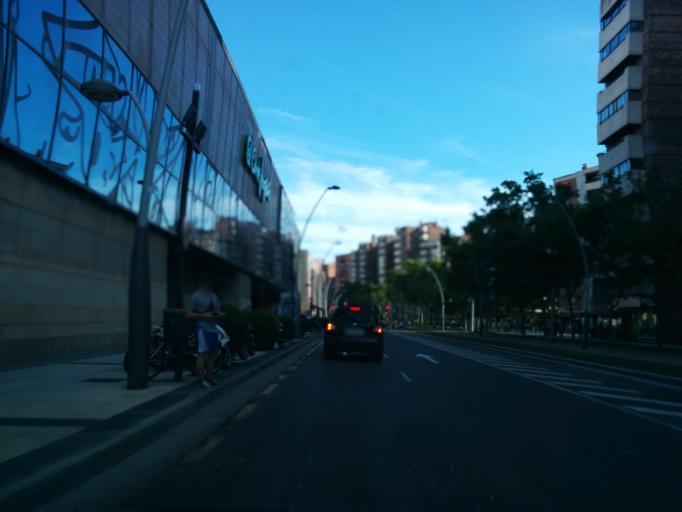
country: ES
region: Aragon
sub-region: Provincia de Zaragoza
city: Almozara
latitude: 41.6723
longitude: -0.8907
